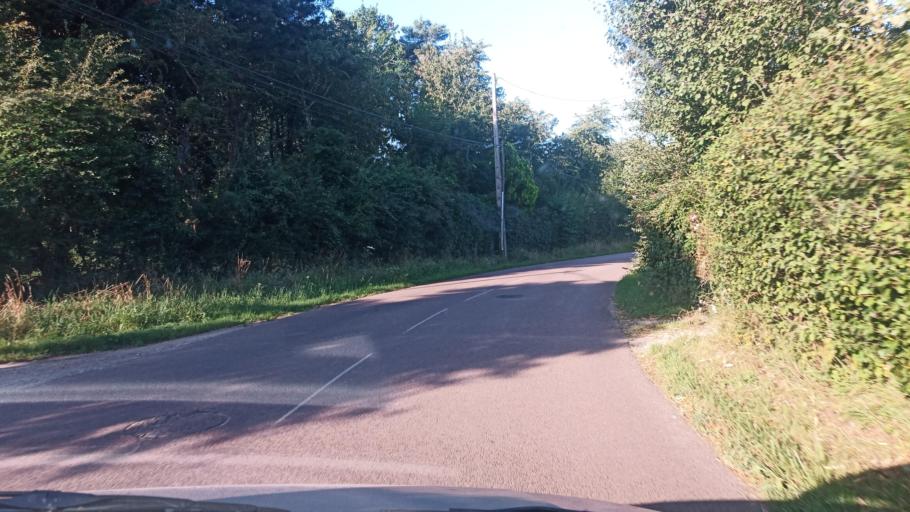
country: FR
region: Bourgogne
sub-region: Departement de l'Yonne
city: Saint-Valerien
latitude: 48.1896
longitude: 3.1151
